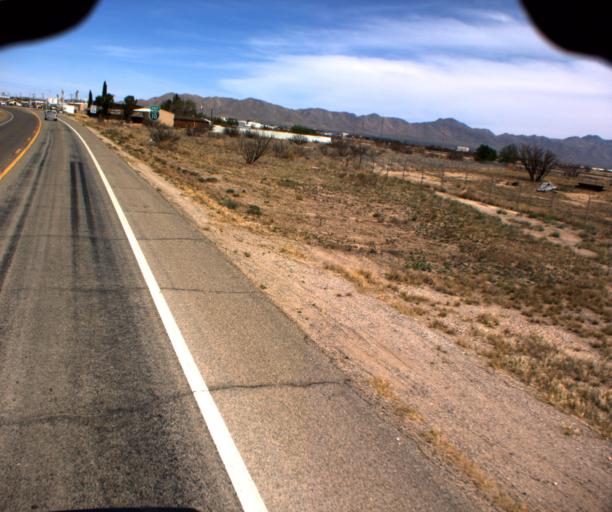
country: US
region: Arizona
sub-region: Cochise County
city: Willcox
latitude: 32.2422
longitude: -109.8398
